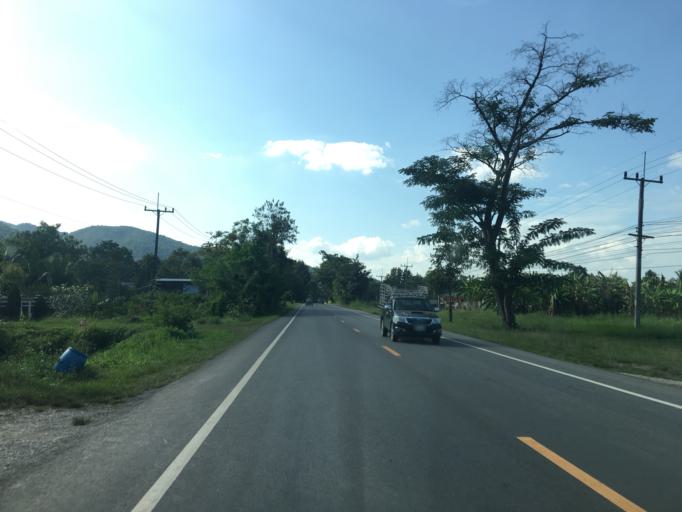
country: TH
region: Phayao
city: Chun
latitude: 19.3508
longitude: 100.1071
